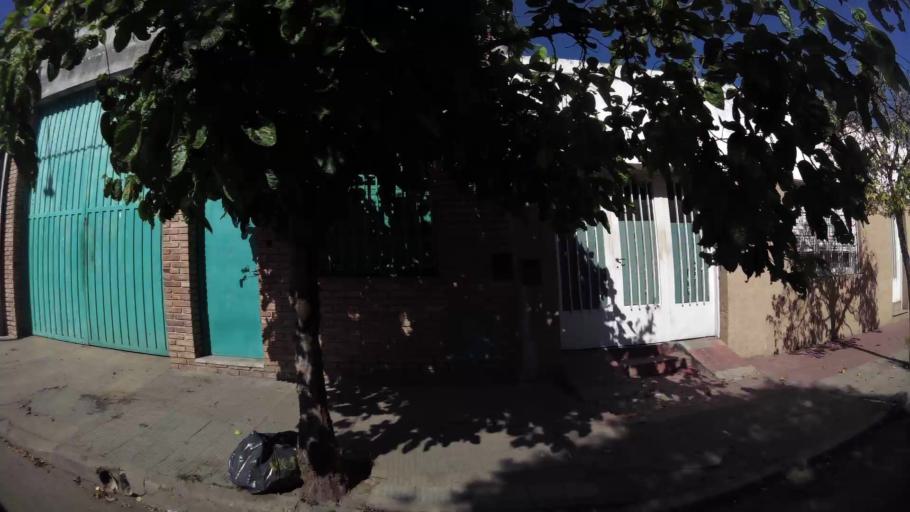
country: AR
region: Cordoba
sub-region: Departamento de Capital
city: Cordoba
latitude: -31.4114
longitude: -64.1501
